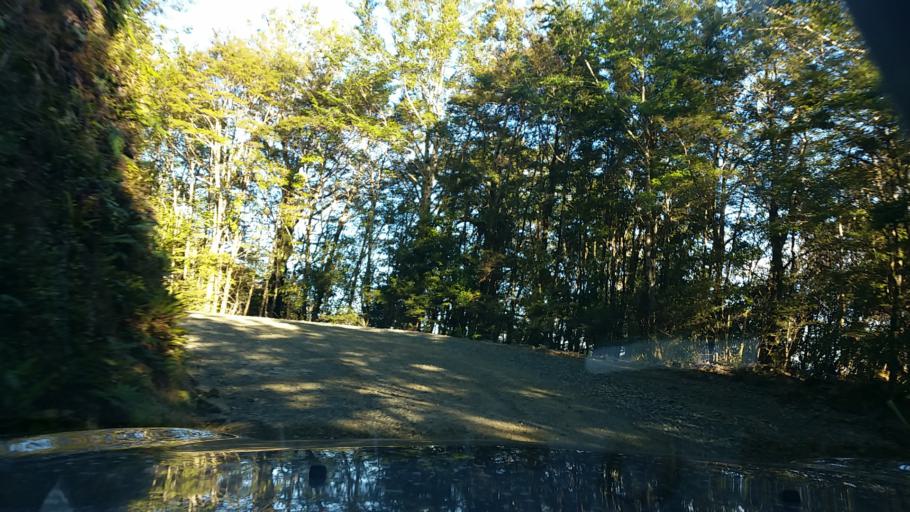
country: NZ
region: Marlborough
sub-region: Marlborough District
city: Picton
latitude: -41.0853
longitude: 174.1508
